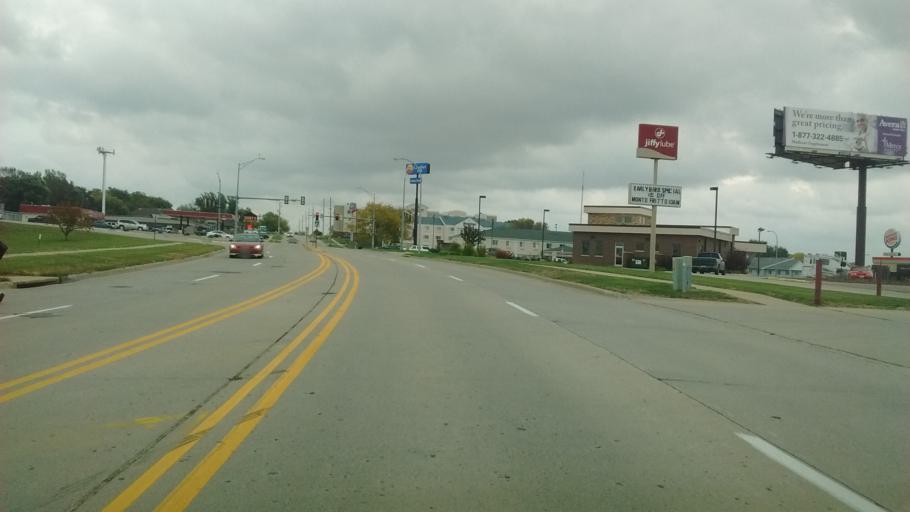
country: US
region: Iowa
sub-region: Woodbury County
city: Sergeant Bluff
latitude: 42.4405
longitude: -96.3495
